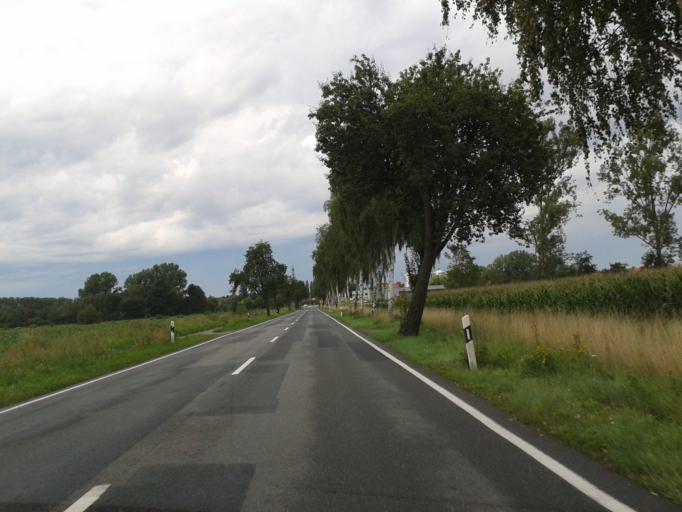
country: DE
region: Lower Saxony
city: Luechow
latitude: 52.9618
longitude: 11.1767
